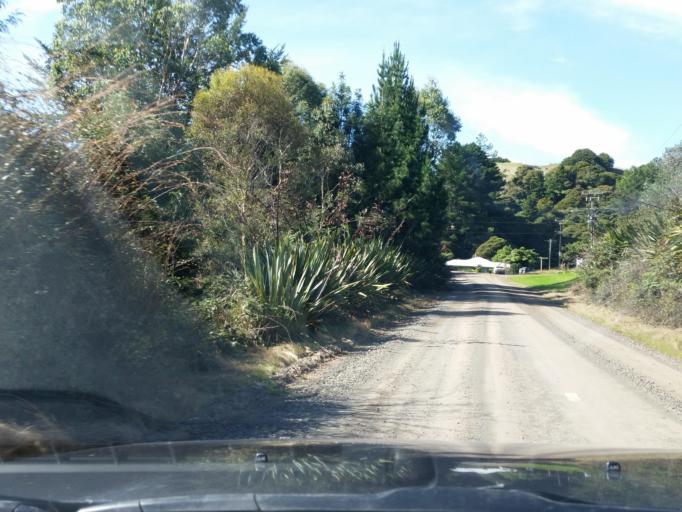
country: NZ
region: Northland
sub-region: Kaipara District
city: Dargaville
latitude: -35.7098
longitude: 173.6211
